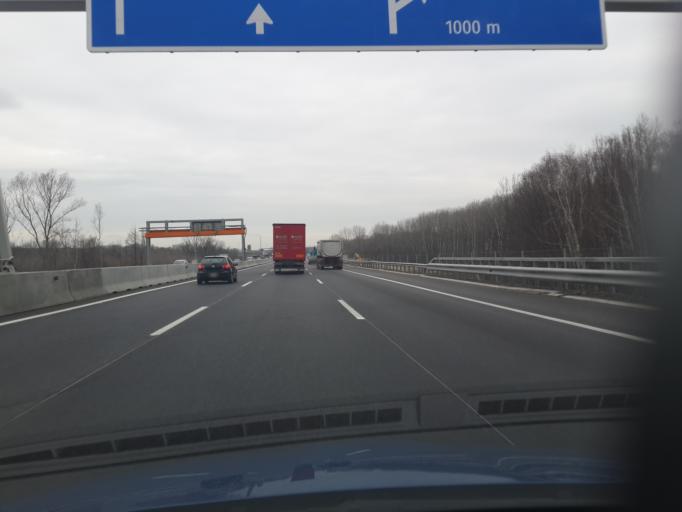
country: AT
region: Lower Austria
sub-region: Politischer Bezirk Wien-Umgebung
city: Fischamend Dorf
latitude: 48.1288
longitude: 16.5644
